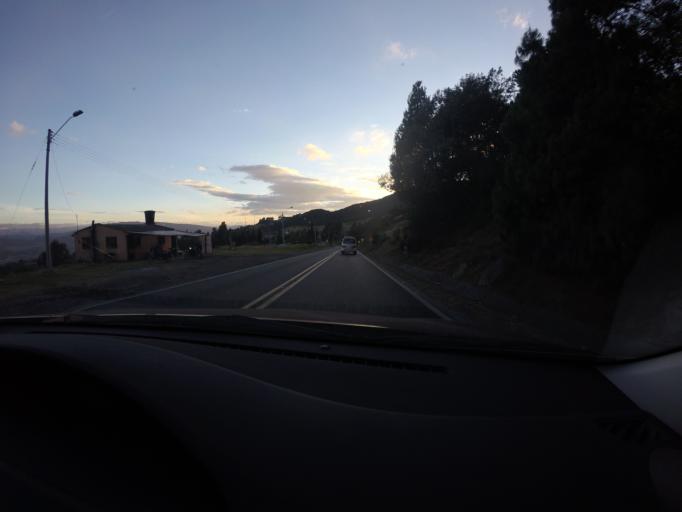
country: CO
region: Cundinamarca
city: Nemocon
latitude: 5.1508
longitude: -73.9022
